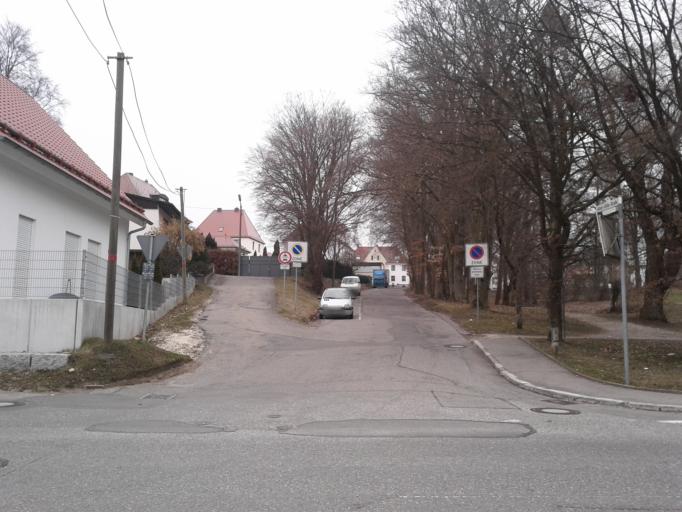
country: DE
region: Bavaria
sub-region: Swabia
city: Guenzburg
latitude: 48.4502
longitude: 10.2774
